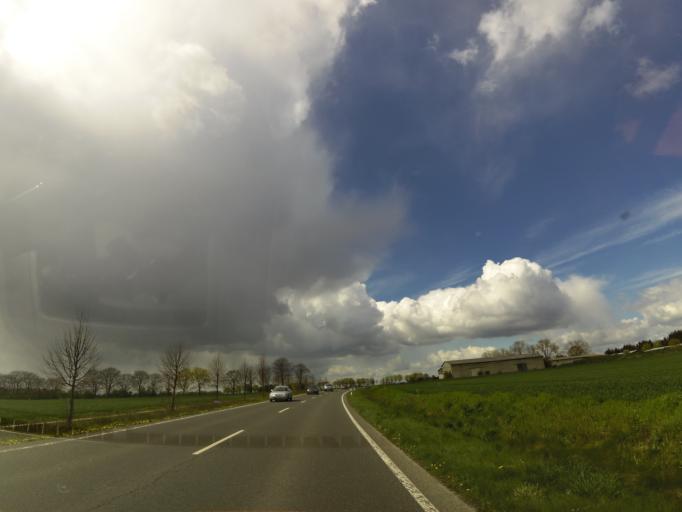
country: DE
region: Saxony-Anhalt
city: Hohendodeleben
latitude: 52.0725
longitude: 11.4879
